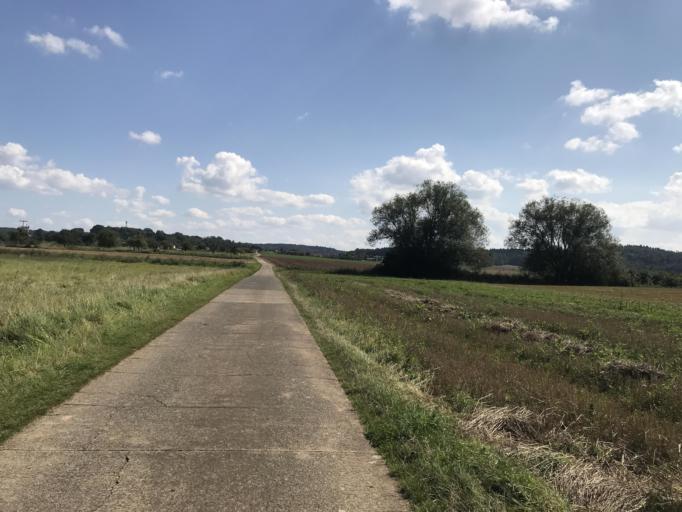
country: DE
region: Hesse
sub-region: Regierungsbezirk Giessen
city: Hungen
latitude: 50.4332
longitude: 8.9045
